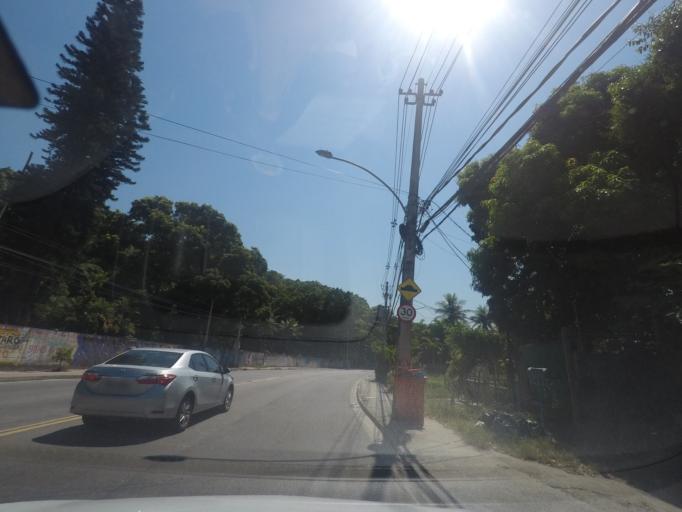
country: BR
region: Rio de Janeiro
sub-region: Nilopolis
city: Nilopolis
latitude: -22.9877
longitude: -43.4849
